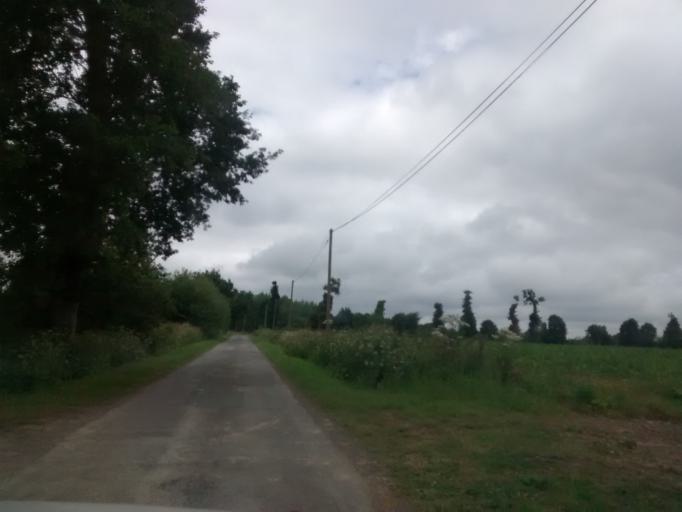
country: FR
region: Brittany
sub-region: Departement d'Ille-et-Vilaine
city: Saint-Gregoire
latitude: 48.1658
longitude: -1.6637
